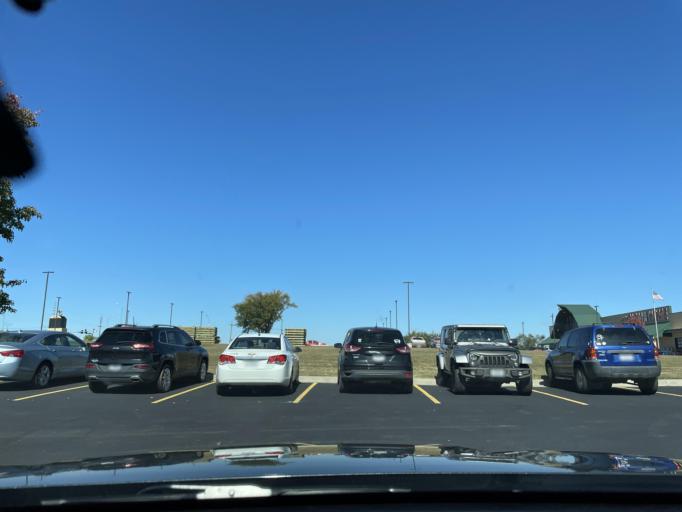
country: US
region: Missouri
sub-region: Buchanan County
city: Saint Joseph
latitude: 39.7537
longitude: -94.7670
